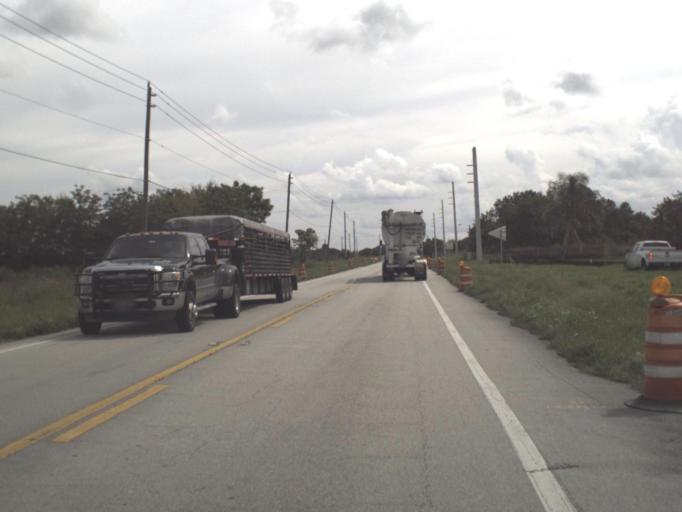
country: US
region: Florida
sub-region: Okeechobee County
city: Taylor Creek
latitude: 27.2577
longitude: -80.7563
